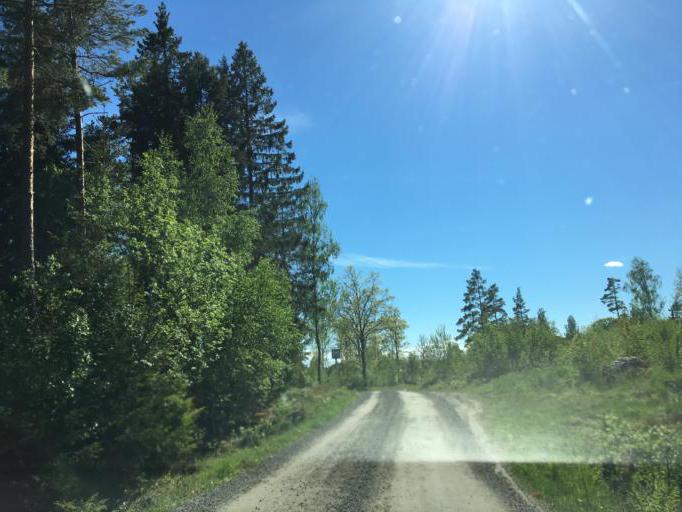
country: SE
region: Soedermanland
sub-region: Eskilstuna Kommun
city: Kvicksund
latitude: 59.3455
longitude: 16.3090
